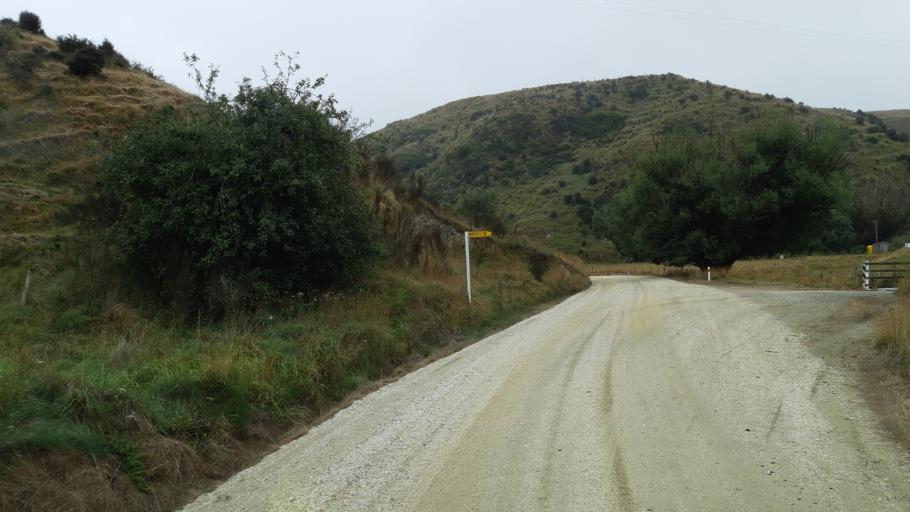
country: NZ
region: Otago
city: Oamaru
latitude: -44.9736
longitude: 170.5140
